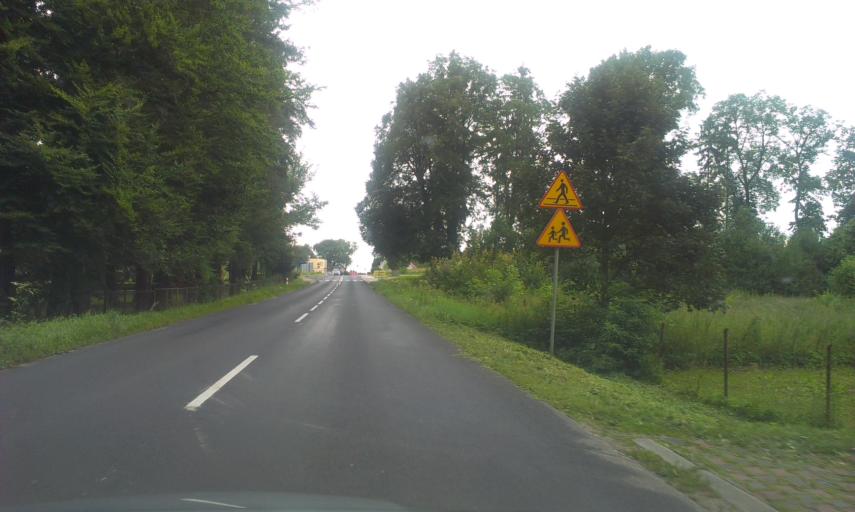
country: PL
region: West Pomeranian Voivodeship
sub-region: Powiat swidwinski
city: Polczyn-Zdroj
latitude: 53.8546
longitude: 16.0725
